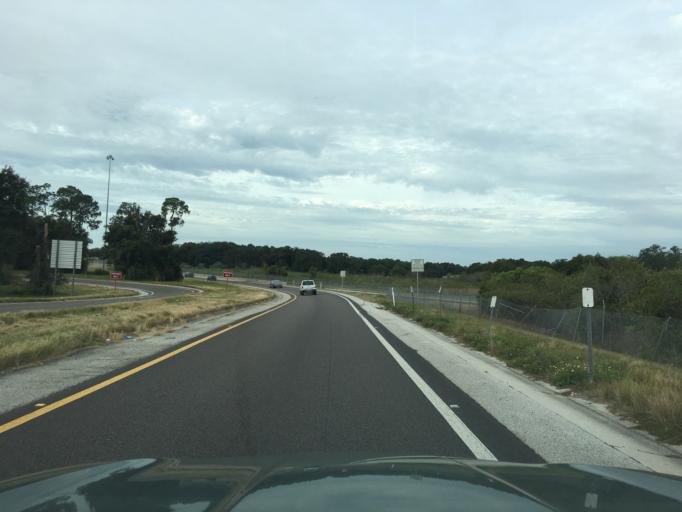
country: US
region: Florida
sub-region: Polk County
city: Winston
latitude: 28.0387
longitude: -82.0566
